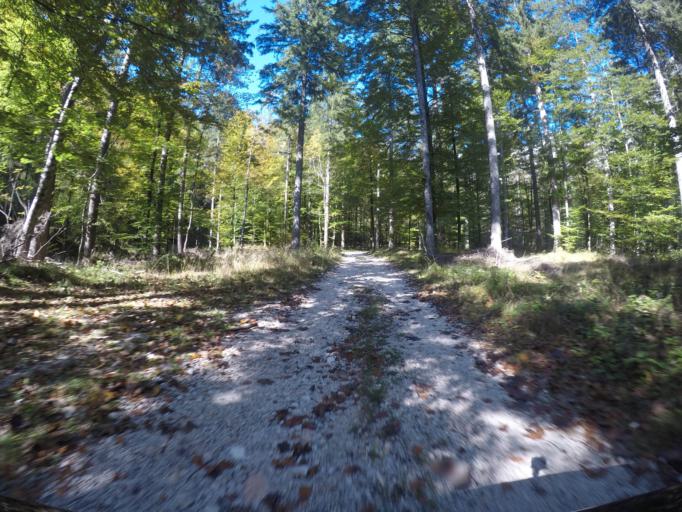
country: SI
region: Kamnik
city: Mekinje
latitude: 46.3276
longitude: 14.5836
